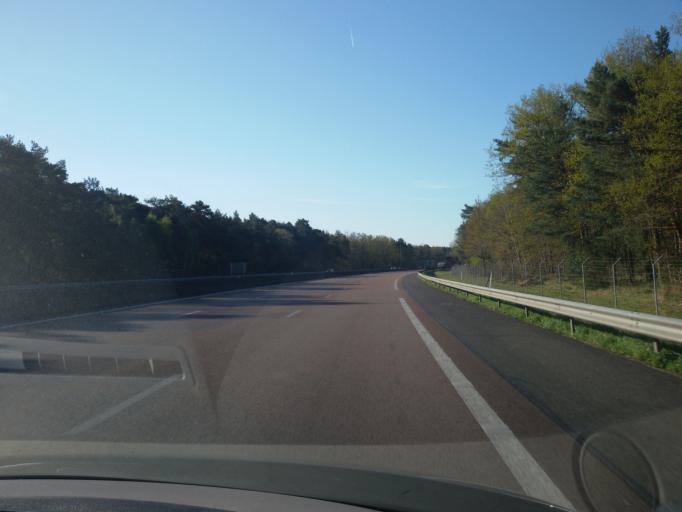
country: FR
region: Ile-de-France
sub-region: Departement de Seine-et-Marne
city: Arbonne-la-Foret
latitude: 48.4065
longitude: 2.5535
